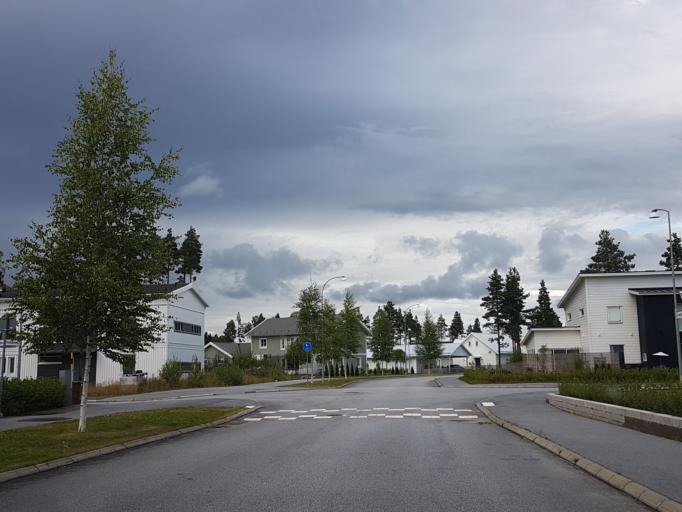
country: SE
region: Vaesterbotten
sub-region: Umea Kommun
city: Ersmark
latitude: 63.8039
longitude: 20.3695
